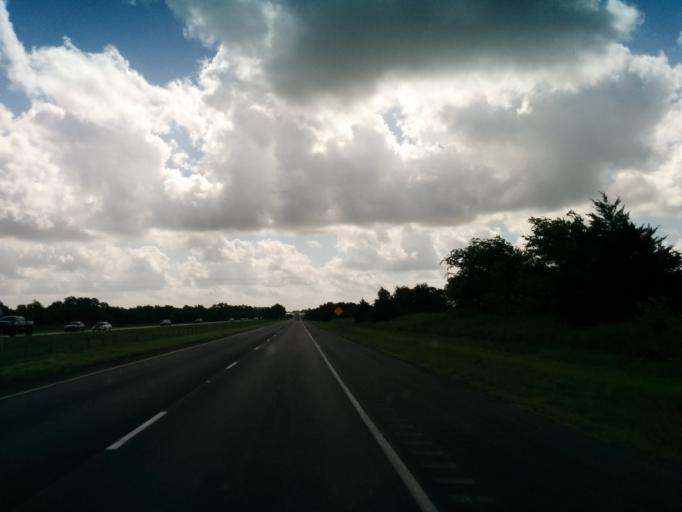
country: US
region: Texas
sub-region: Fayette County
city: Schulenburg
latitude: 29.6960
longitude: -96.8788
